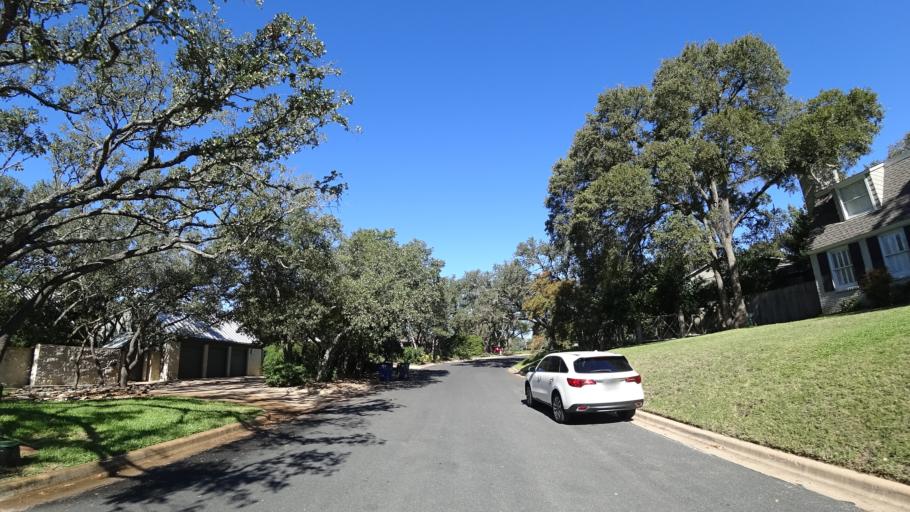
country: US
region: Texas
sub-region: Travis County
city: West Lake Hills
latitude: 30.3596
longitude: -97.7708
